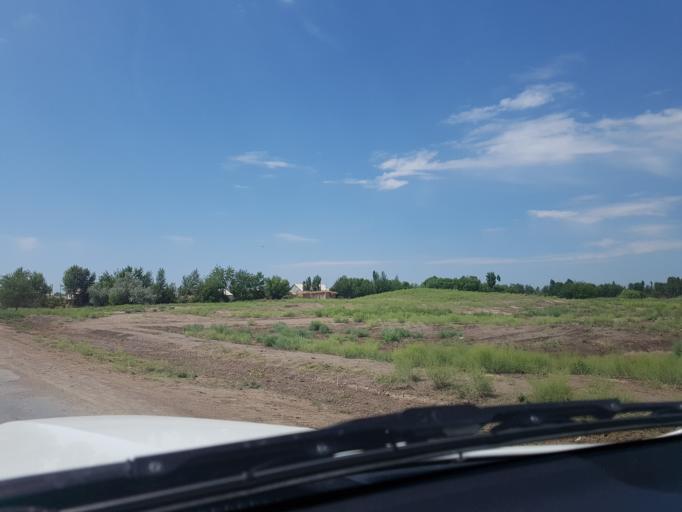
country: TM
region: Dasoguz
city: Koeneuergench
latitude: 42.3178
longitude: 59.1395
